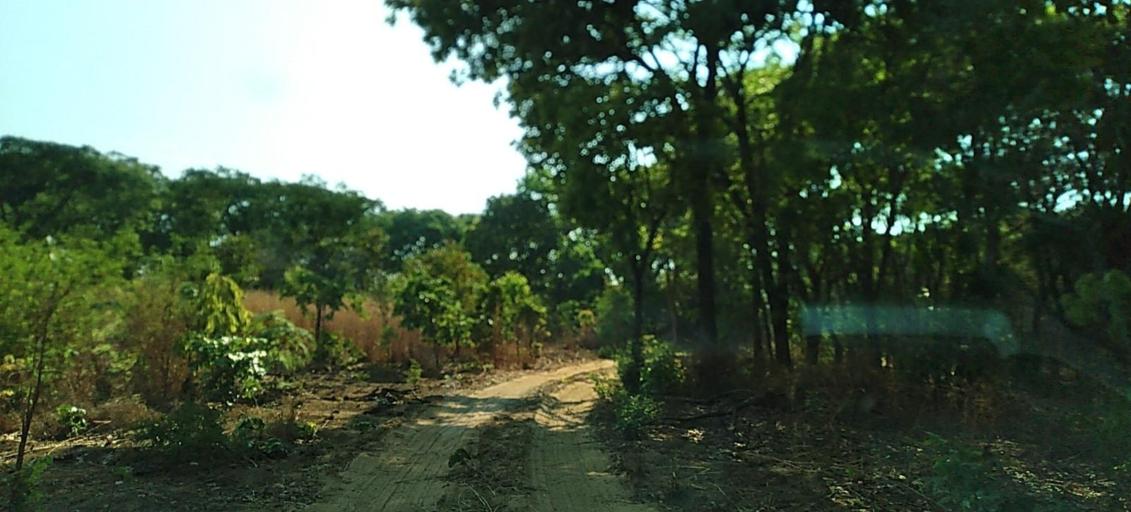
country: ZM
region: Copperbelt
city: Kalulushi
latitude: -13.0046
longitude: 27.7599
